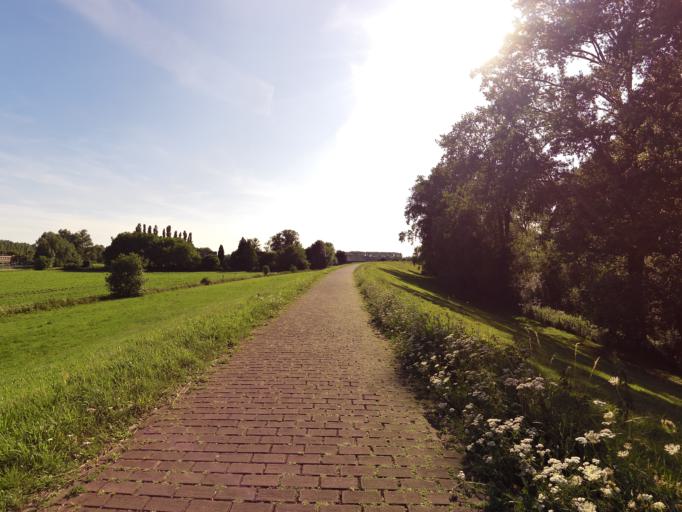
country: DE
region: North Rhine-Westphalia
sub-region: Regierungsbezirk Dusseldorf
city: Kranenburg
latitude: 51.8647
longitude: 6.0191
